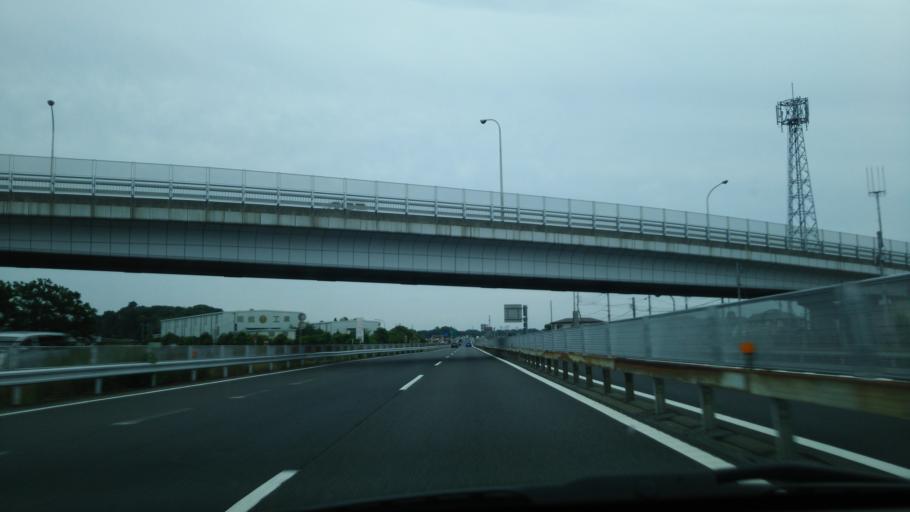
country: JP
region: Kanagawa
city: Isehara
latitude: 35.3647
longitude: 139.3076
